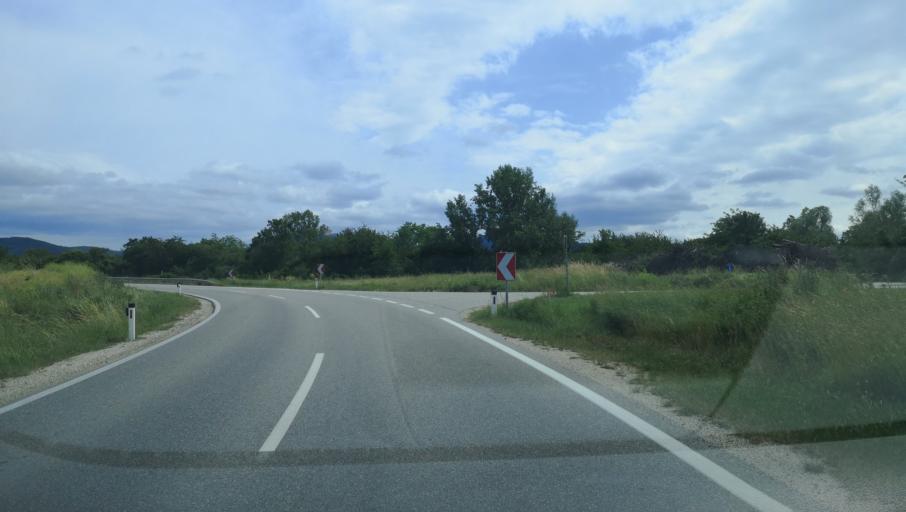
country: AT
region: Lower Austria
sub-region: Politischer Bezirk Krems
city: Weinzierl bei Krems
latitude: 48.3942
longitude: 15.5958
